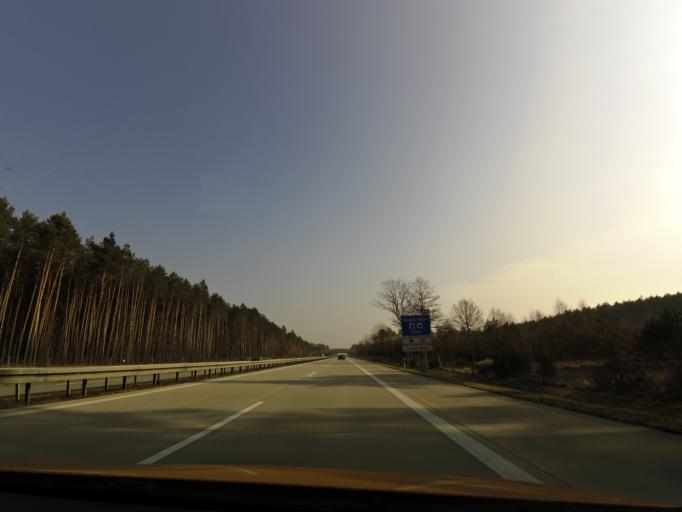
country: DE
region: Brandenburg
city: Briesen
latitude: 52.3235
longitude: 14.3068
